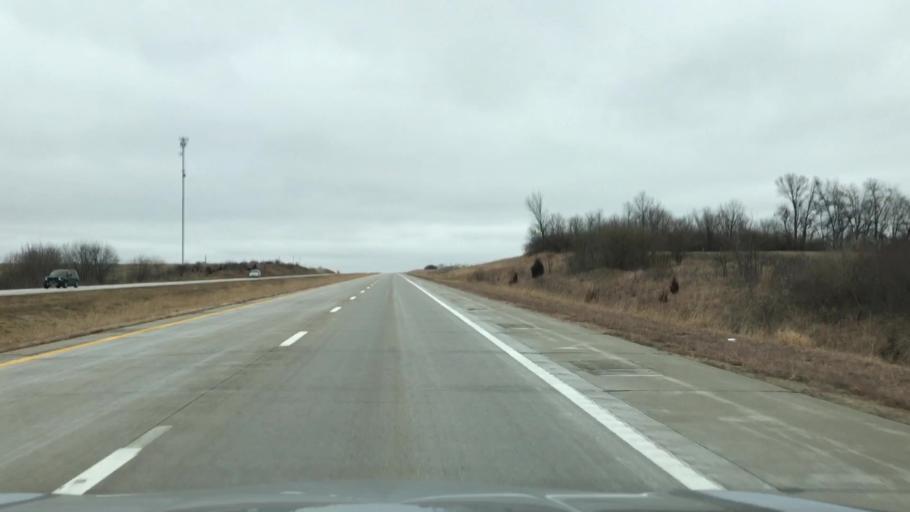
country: US
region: Missouri
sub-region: Caldwell County
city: Hamilton
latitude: 39.7348
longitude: -93.7748
